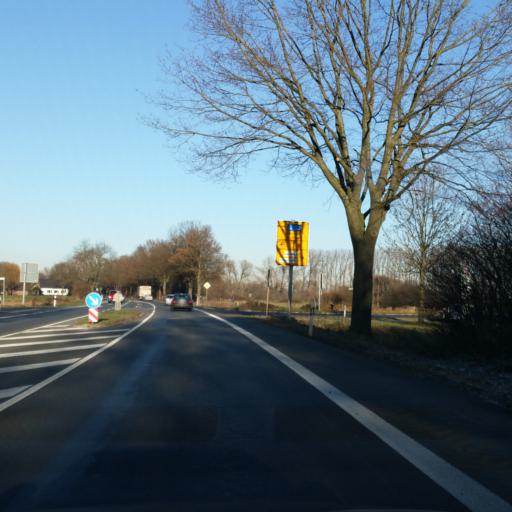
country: DE
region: North Rhine-Westphalia
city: Rees
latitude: 51.7824
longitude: 6.4061
